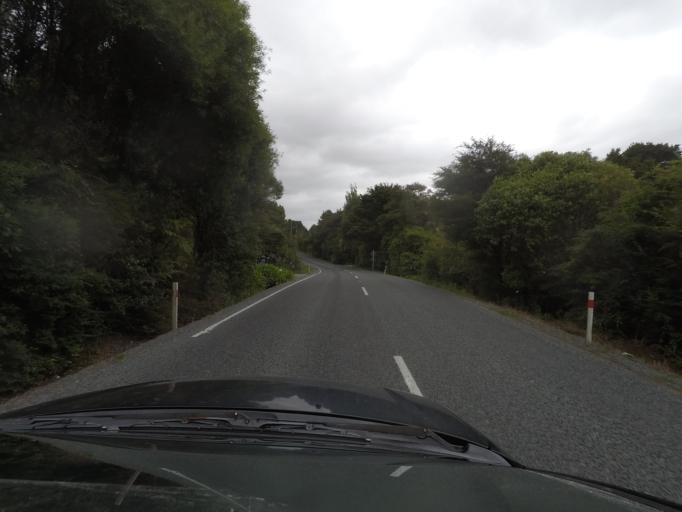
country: NZ
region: Auckland
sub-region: Auckland
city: Wellsford
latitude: -36.2805
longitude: 174.5898
